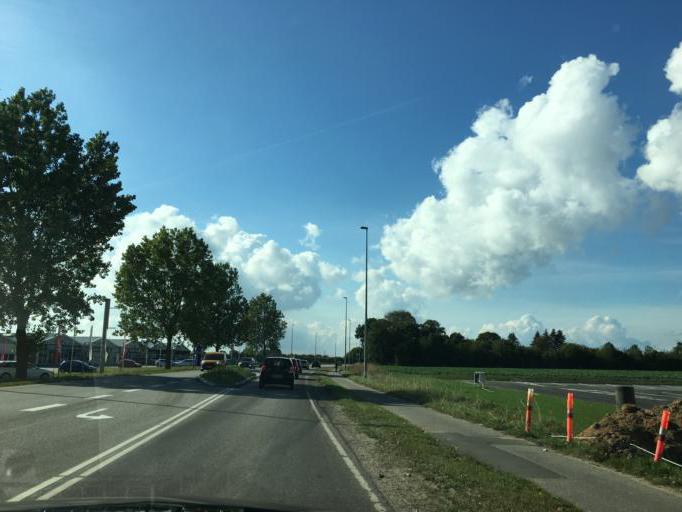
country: DK
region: South Denmark
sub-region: Fredericia Kommune
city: Snoghoj
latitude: 55.5678
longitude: 9.7010
